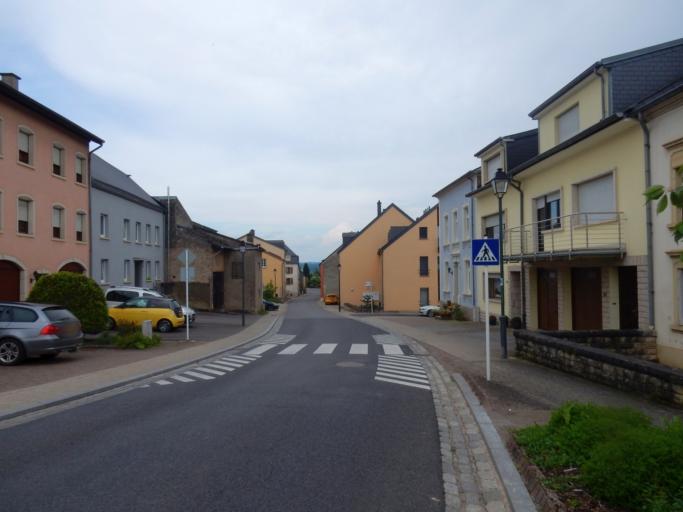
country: LU
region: Grevenmacher
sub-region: Canton de Remich
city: Bous
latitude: 49.5238
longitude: 6.3392
